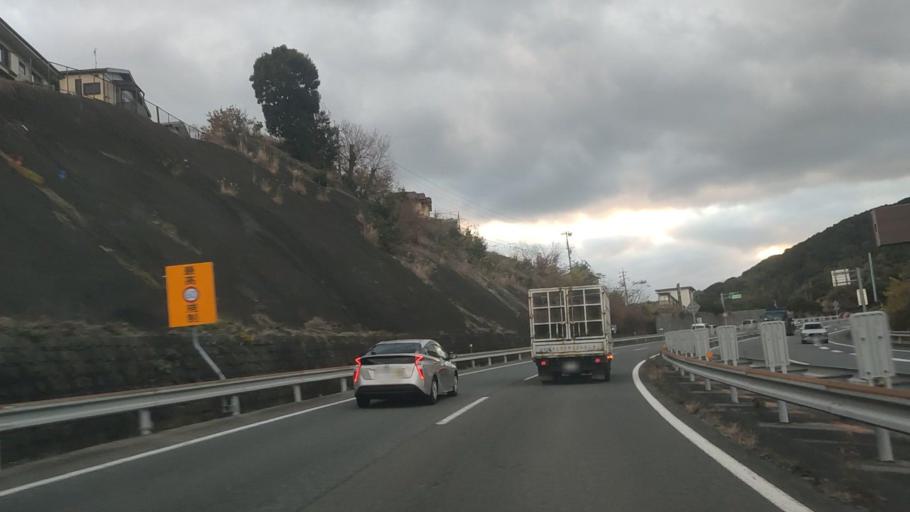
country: JP
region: Nagasaki
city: Obita
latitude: 32.8123
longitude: 129.9617
